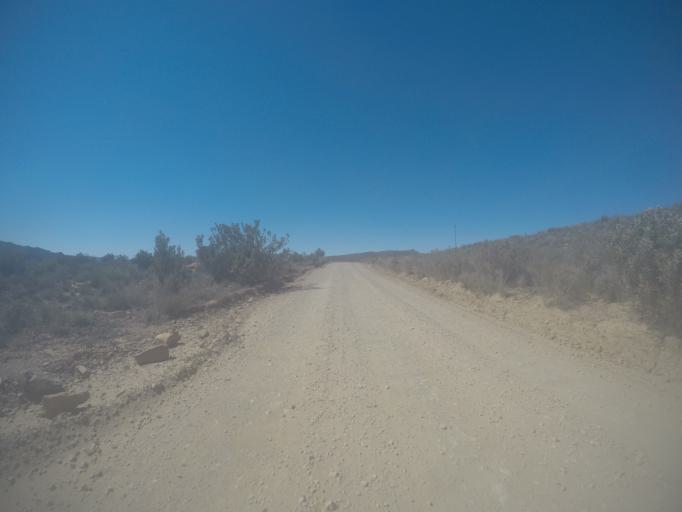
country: ZA
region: Western Cape
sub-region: West Coast District Municipality
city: Clanwilliam
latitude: -32.4985
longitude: 19.2750
